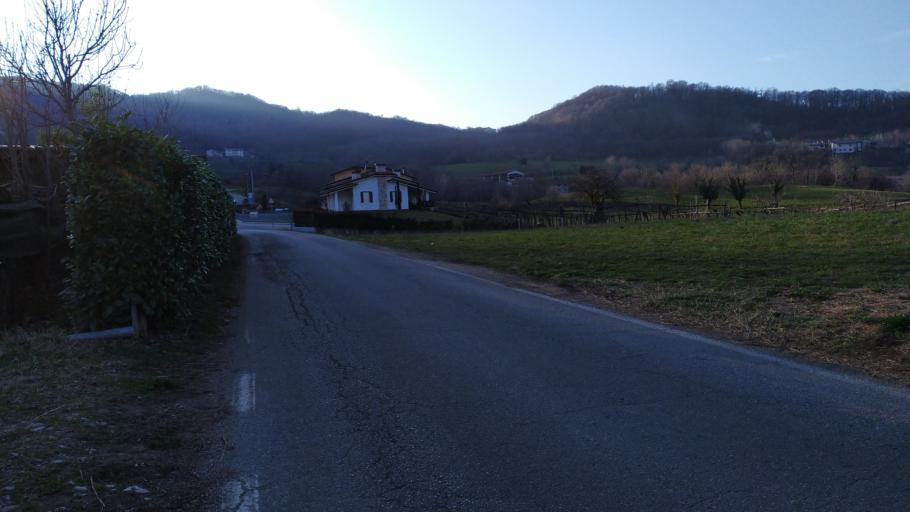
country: IT
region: Veneto
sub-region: Provincia di Vicenza
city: Monte di Malo
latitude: 45.6616
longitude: 11.3552
